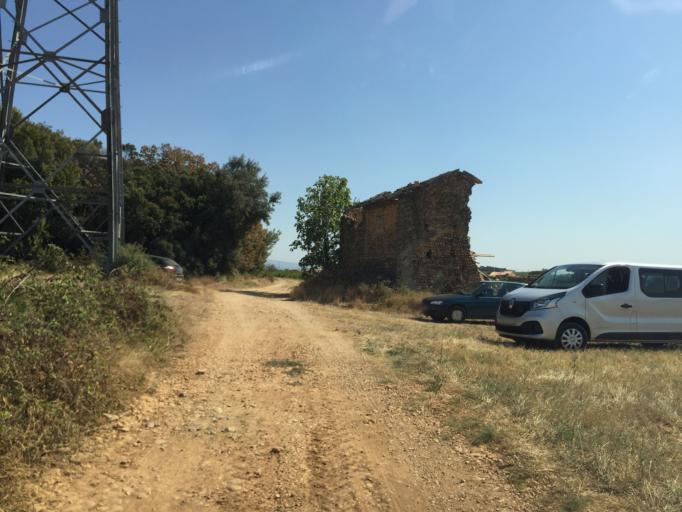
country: FR
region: Provence-Alpes-Cote d'Azur
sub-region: Departement du Vaucluse
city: Orange
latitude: 44.1073
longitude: 4.8351
